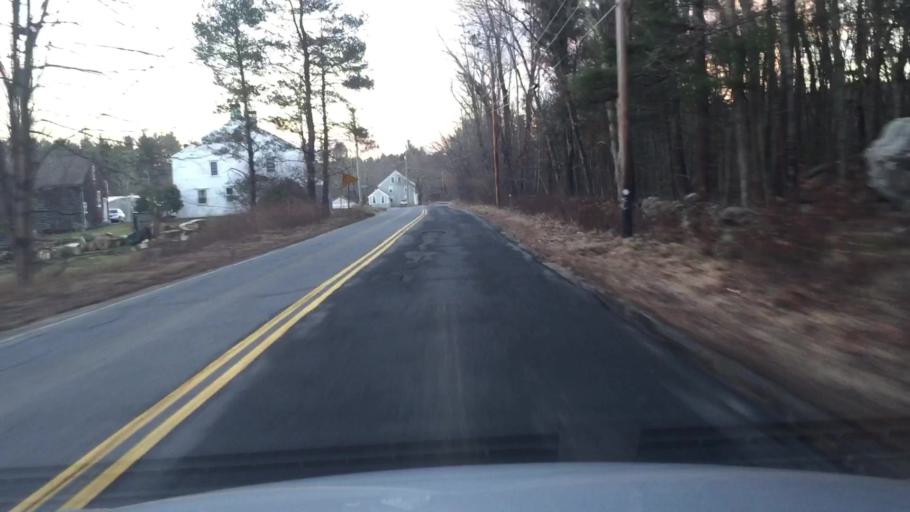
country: US
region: Massachusetts
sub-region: Worcester County
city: Princeton
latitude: 42.4378
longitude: -71.8202
